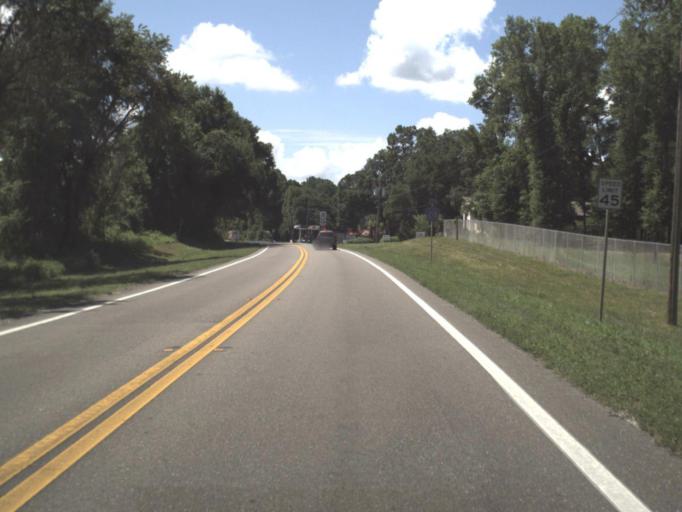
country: US
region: Florida
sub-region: Clay County
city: Keystone Heights
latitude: 29.7577
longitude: -82.0570
